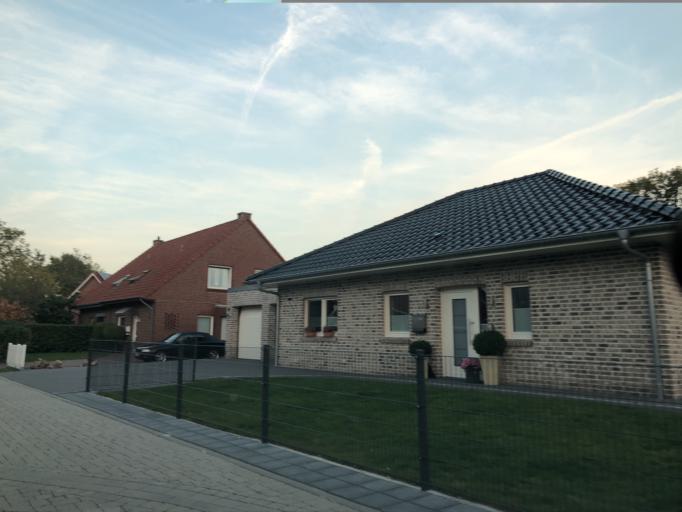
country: DE
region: Lower Saxony
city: Papenburg
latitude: 53.0692
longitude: 7.4278
